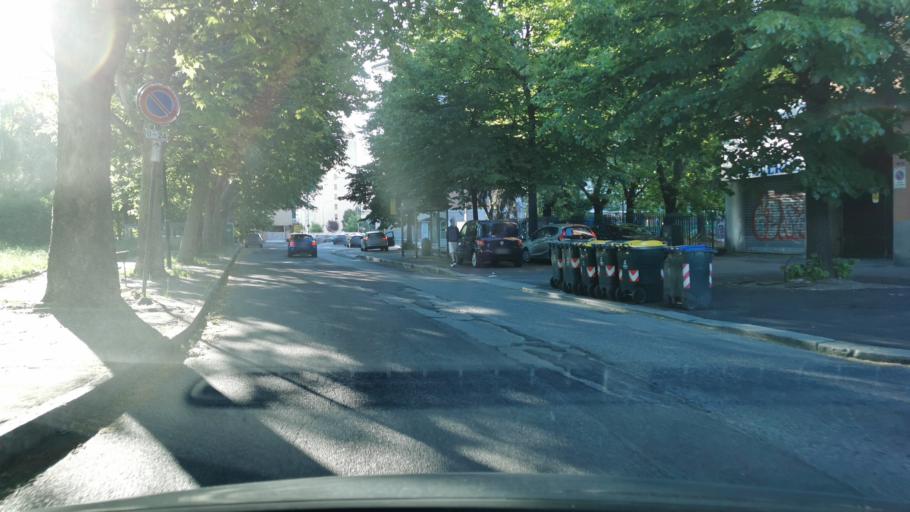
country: IT
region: Piedmont
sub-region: Provincia di Torino
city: Venaria Reale
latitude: 45.1053
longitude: 7.6549
